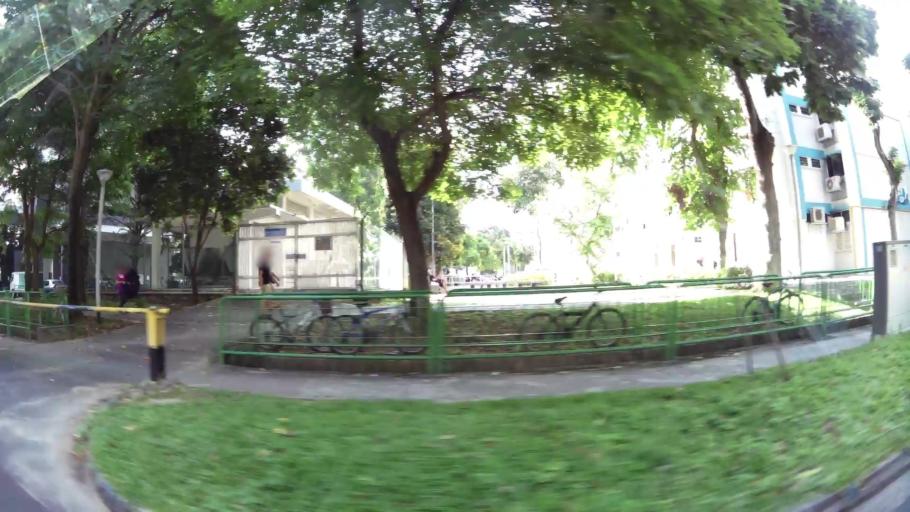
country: SG
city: Singapore
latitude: 1.3184
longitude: 103.8800
